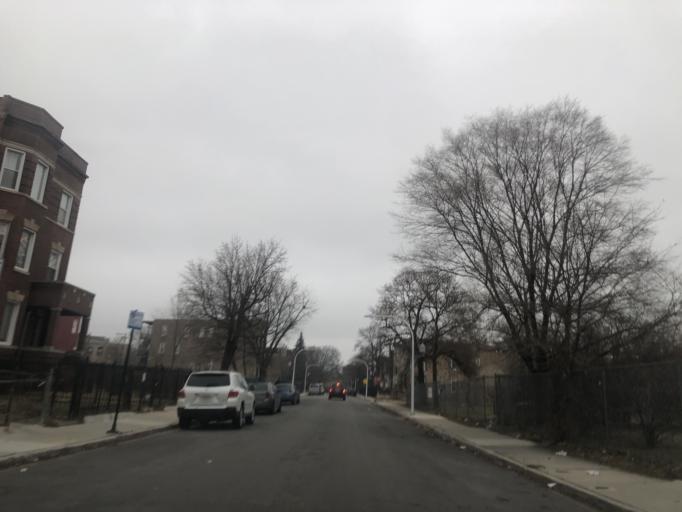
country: US
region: Illinois
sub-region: Cook County
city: Chicago
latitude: 41.7778
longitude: -87.6028
